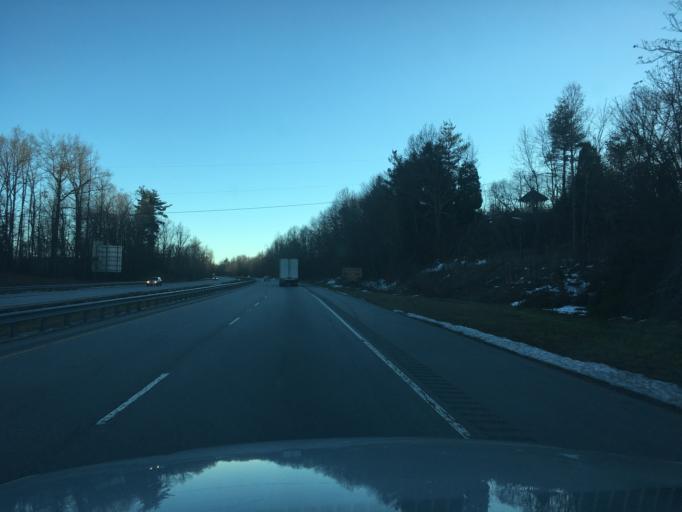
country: US
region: North Carolina
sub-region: Henderson County
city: East Flat Rock
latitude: 35.2492
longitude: -82.4113
